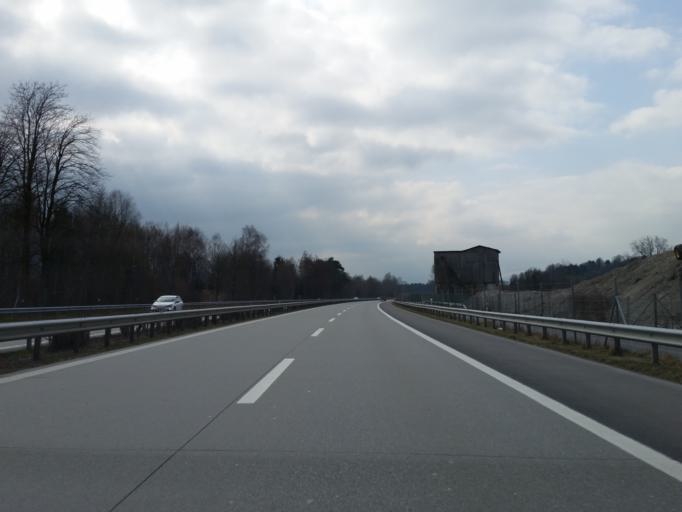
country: CH
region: Saint Gallen
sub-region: Wahlkreis Rheintal
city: Ruthi
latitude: 47.2894
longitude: 9.5506
